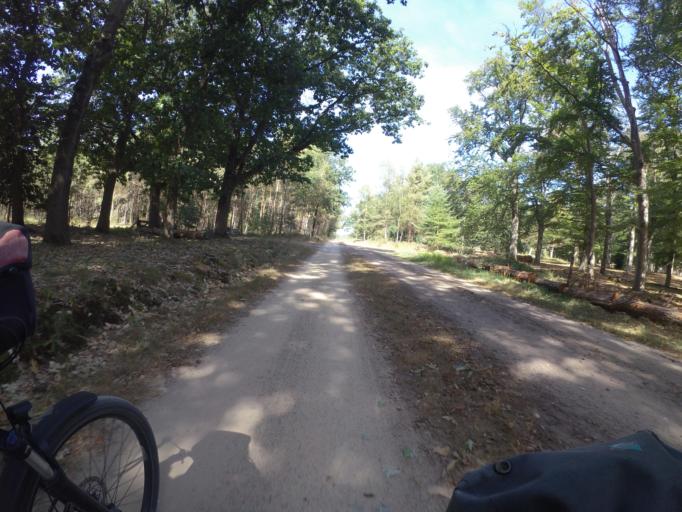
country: NL
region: Overijssel
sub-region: Gemeente Raalte
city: Raalte
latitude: 52.3361
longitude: 6.3855
